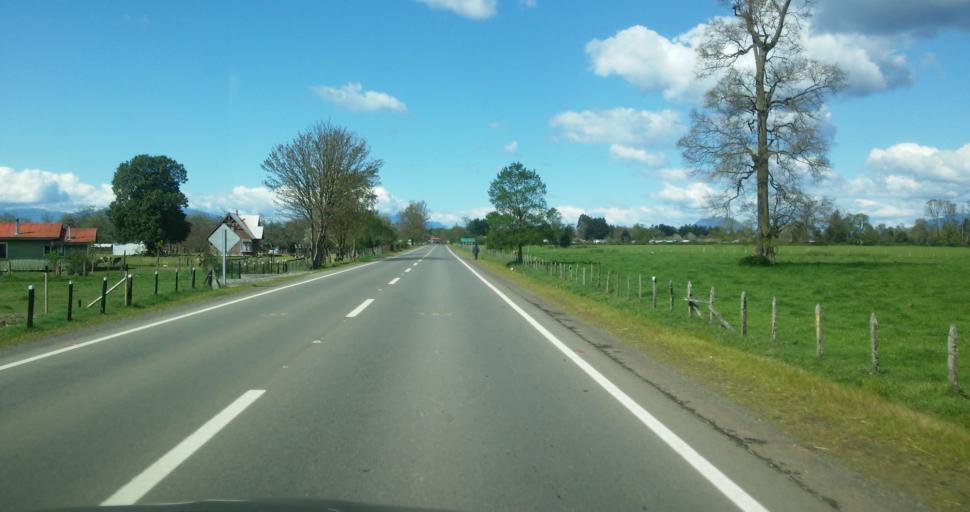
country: CL
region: Los Rios
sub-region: Provincia del Ranco
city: Rio Bueno
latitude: -40.2401
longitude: -72.6018
